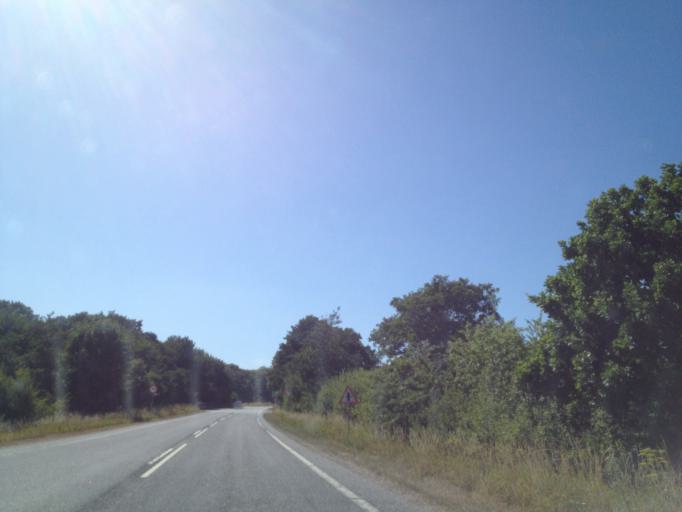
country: DK
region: Capital Region
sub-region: Fredensborg Kommune
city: Fredensborg
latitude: 56.0426
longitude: 12.3812
